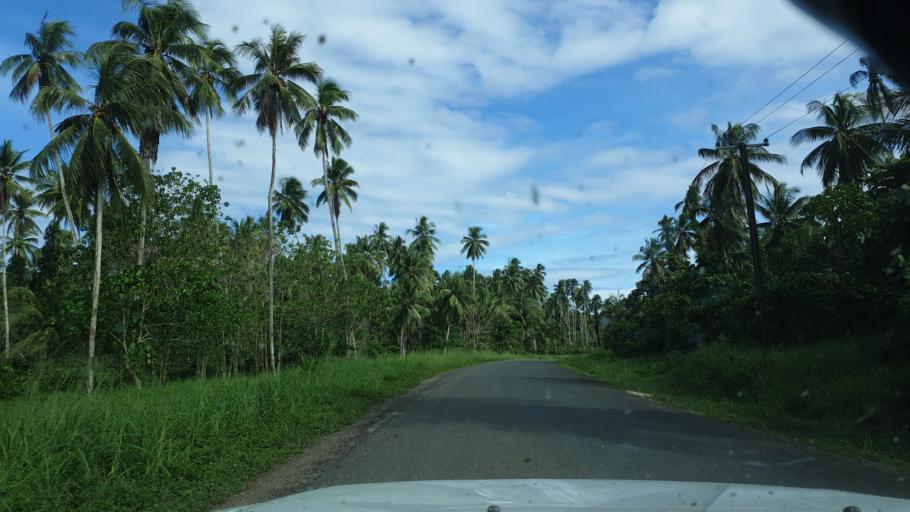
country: PG
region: Madang
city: Madang
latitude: -4.9830
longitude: 145.7849
